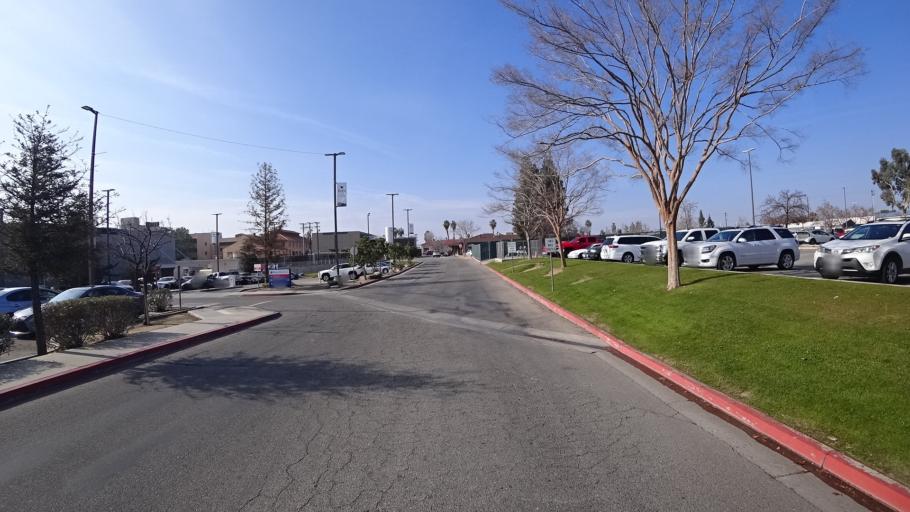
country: US
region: California
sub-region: Kern County
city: Bakersfield
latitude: 35.3832
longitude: -118.9690
